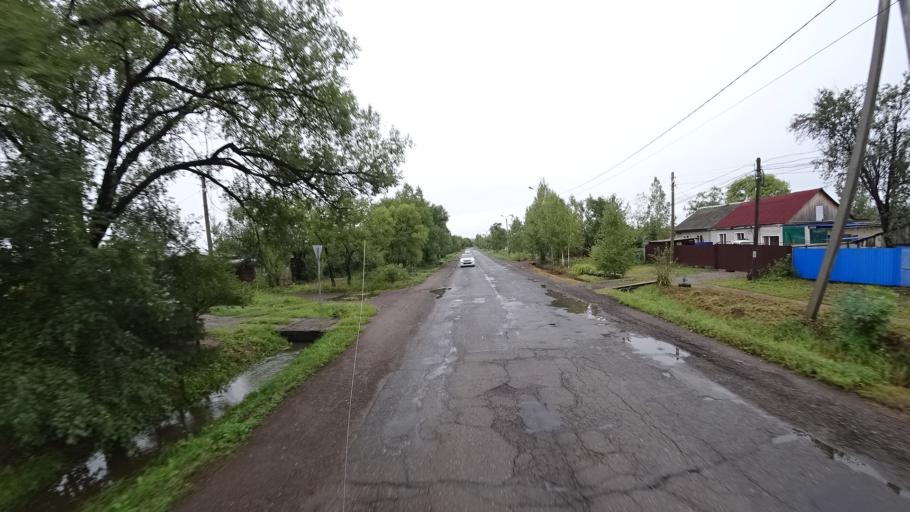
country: RU
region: Primorskiy
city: Monastyrishche
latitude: 44.2001
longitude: 132.4588
